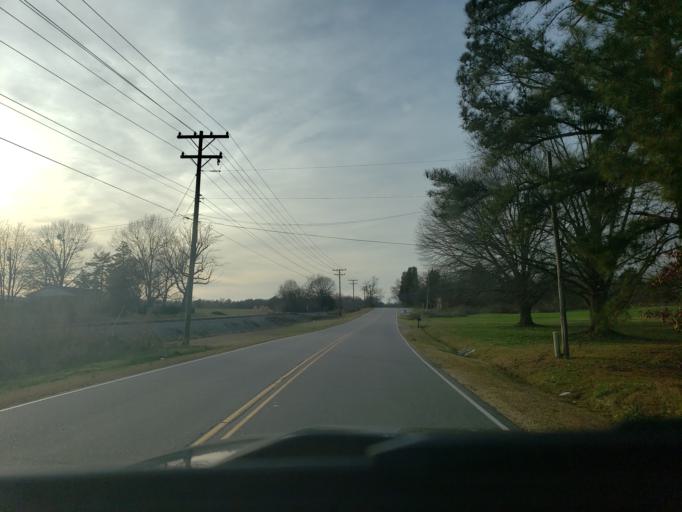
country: US
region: North Carolina
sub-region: Cleveland County
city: Boiling Springs
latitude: 35.3042
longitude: -81.7169
